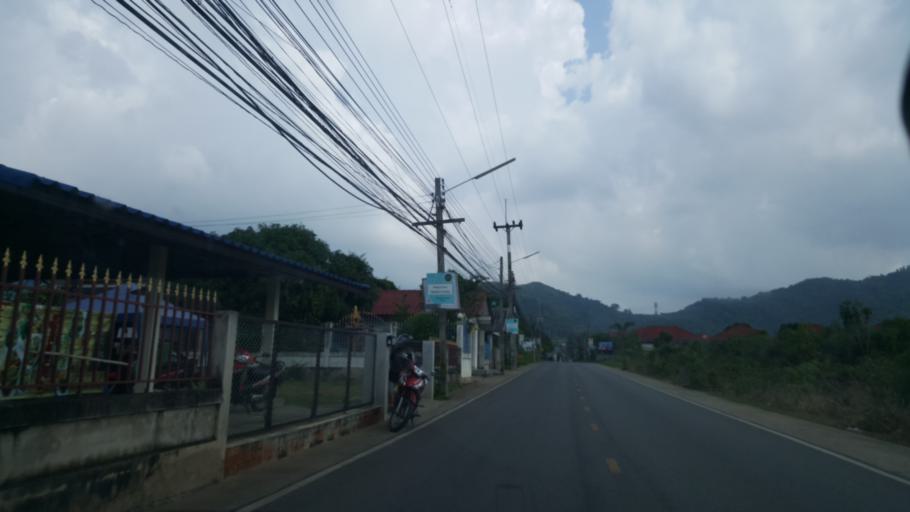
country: TH
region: Chon Buri
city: Sattahip
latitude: 12.6888
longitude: 100.9066
